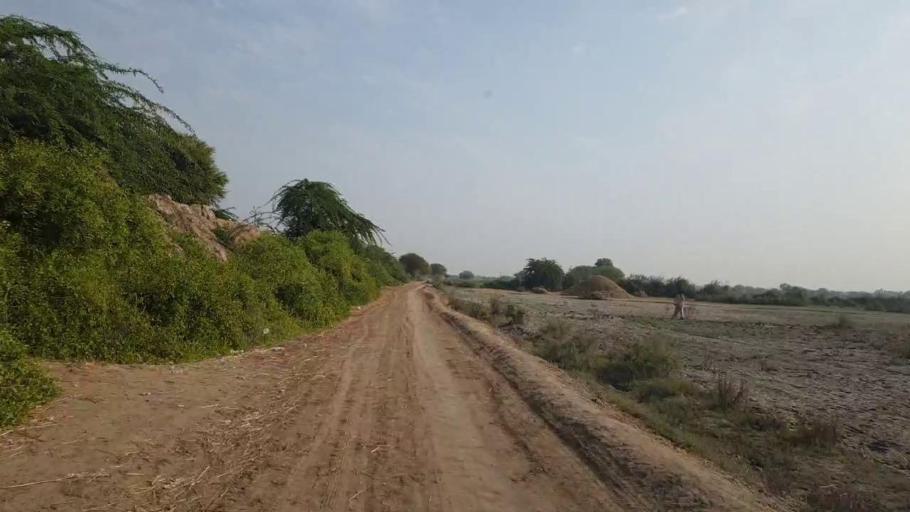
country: PK
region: Sindh
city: Talhar
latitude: 24.8990
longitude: 68.8906
